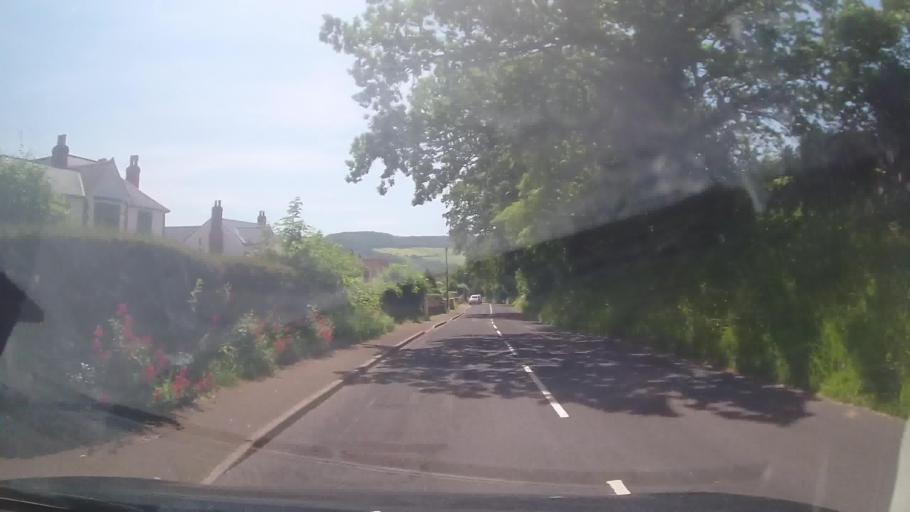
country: GB
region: Wales
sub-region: Monmouthshire
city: Monmouth
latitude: 51.8250
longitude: -2.7126
